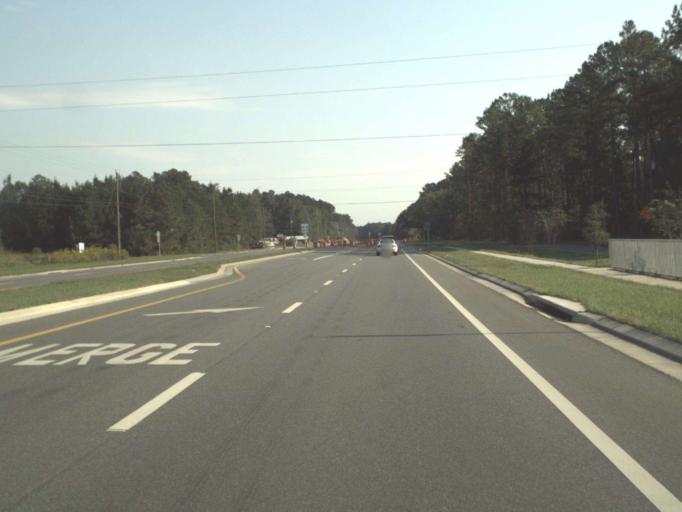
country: US
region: Florida
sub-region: Holmes County
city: Bonifay
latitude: 30.6317
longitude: -85.7104
